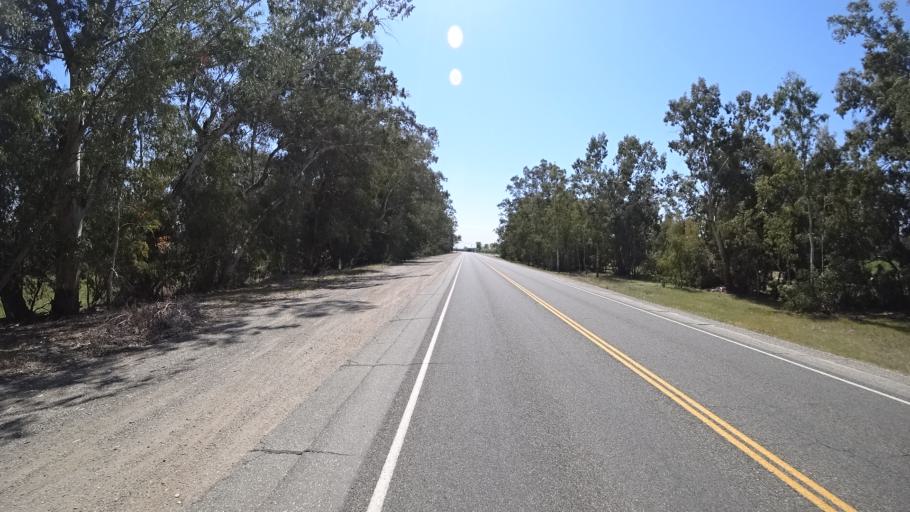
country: US
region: California
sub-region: Glenn County
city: Willows
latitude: 39.5878
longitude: -122.1946
